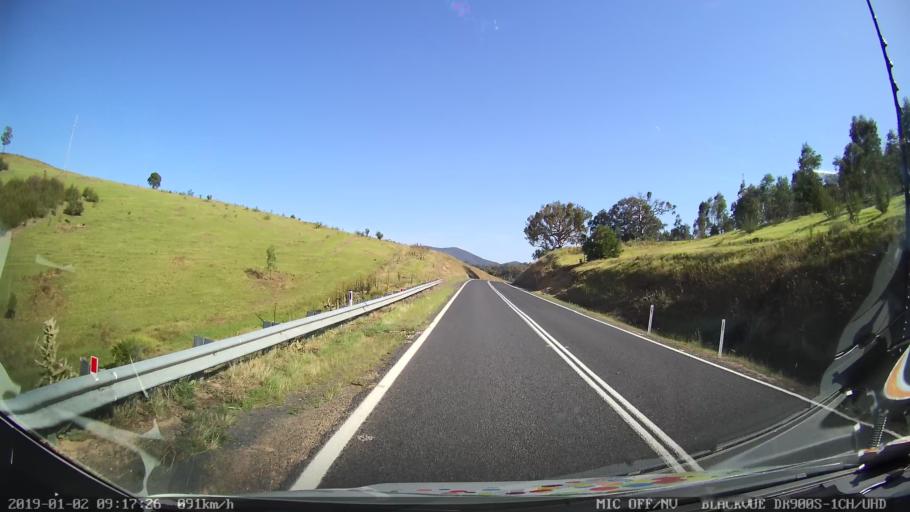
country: AU
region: New South Wales
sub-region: Tumut Shire
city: Tumut
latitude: -35.4404
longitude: 148.2867
